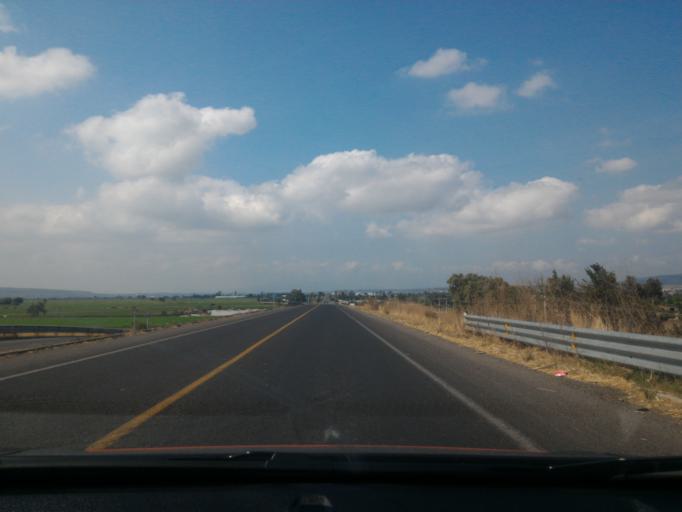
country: MX
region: Guanajuato
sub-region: Penjamo
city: Estacion la Piedad
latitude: 20.3967
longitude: -101.9996
